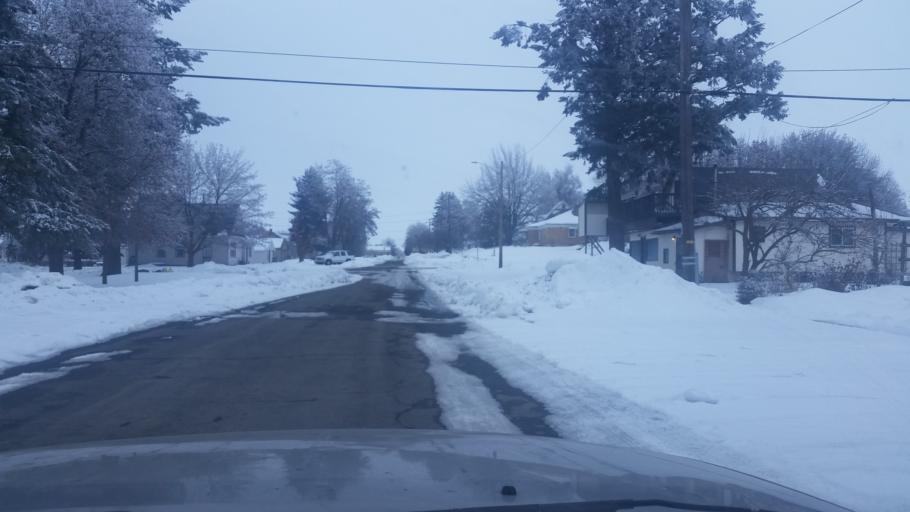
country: US
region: Washington
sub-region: Spokane County
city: Medical Lake
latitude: 47.6673
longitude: -117.8829
